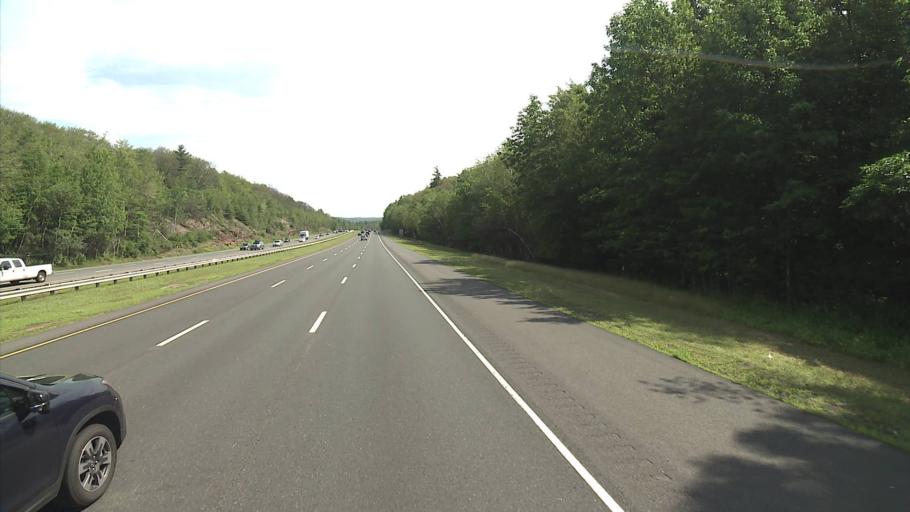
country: US
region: Massachusetts
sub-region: Hampden County
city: Holland
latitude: 42.0111
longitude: -72.1584
